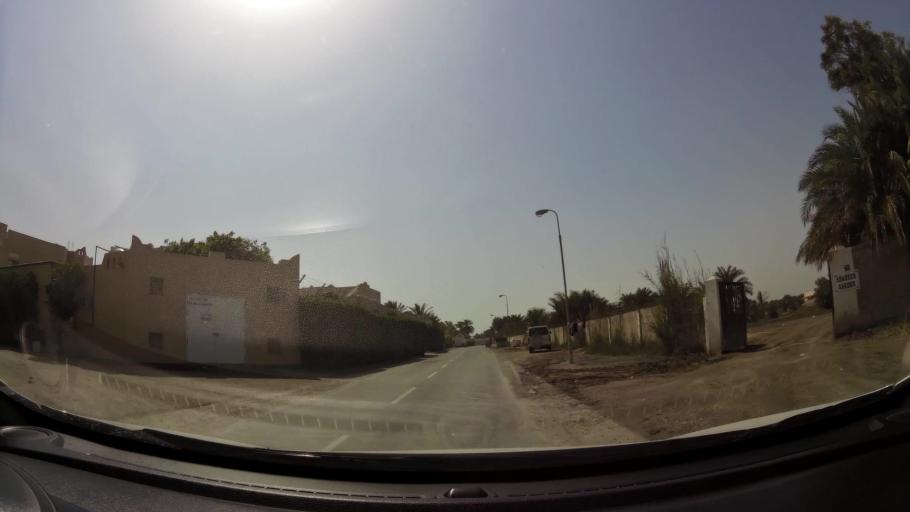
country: BH
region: Northern
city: Madinat `Isa
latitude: 26.1935
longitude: 50.4598
